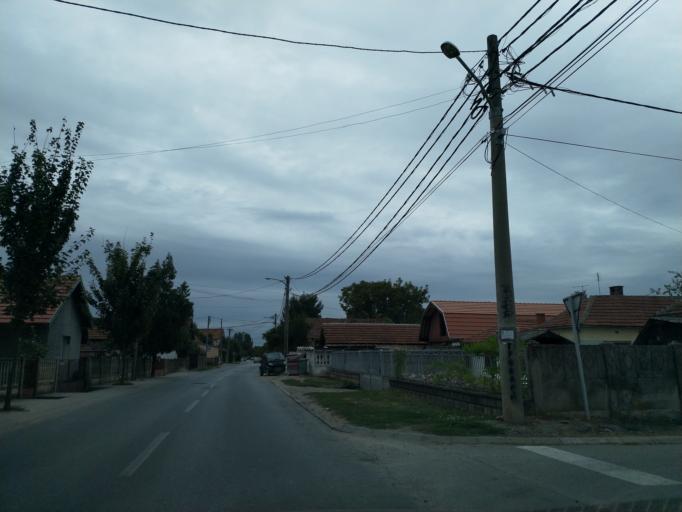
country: RS
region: Central Serbia
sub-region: Pomoravski Okrug
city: Paracin
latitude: 43.8558
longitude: 21.3976
